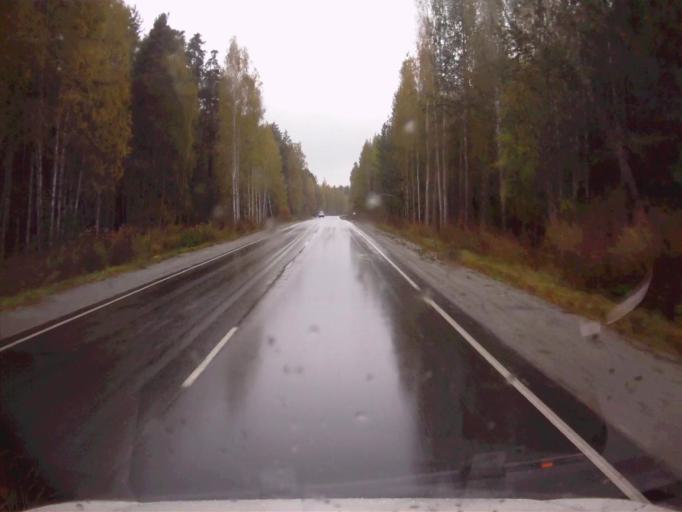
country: RU
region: Chelyabinsk
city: Kyshtym
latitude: 55.6514
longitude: 60.5788
